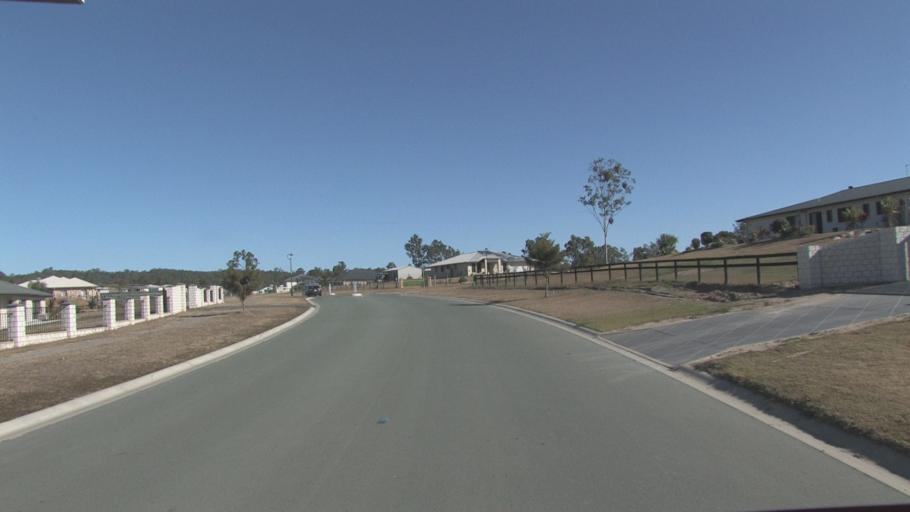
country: AU
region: Queensland
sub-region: Logan
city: Cedar Vale
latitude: -27.8680
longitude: 153.0490
